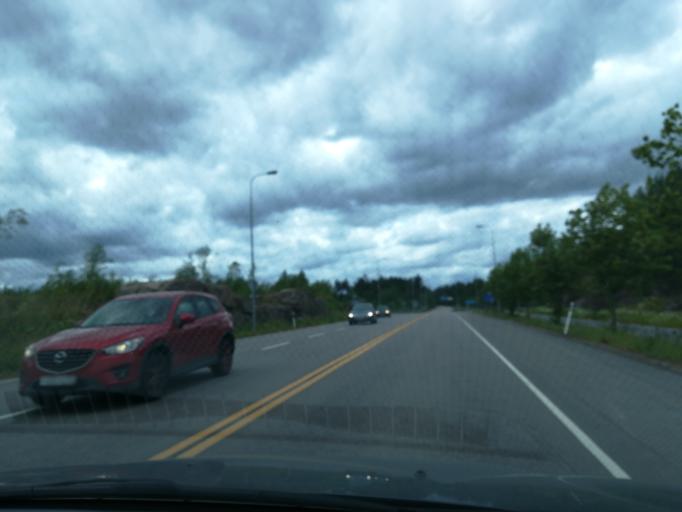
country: FI
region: South Karelia
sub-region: Lappeenranta
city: Lappeenranta
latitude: 61.0654
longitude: 28.2963
